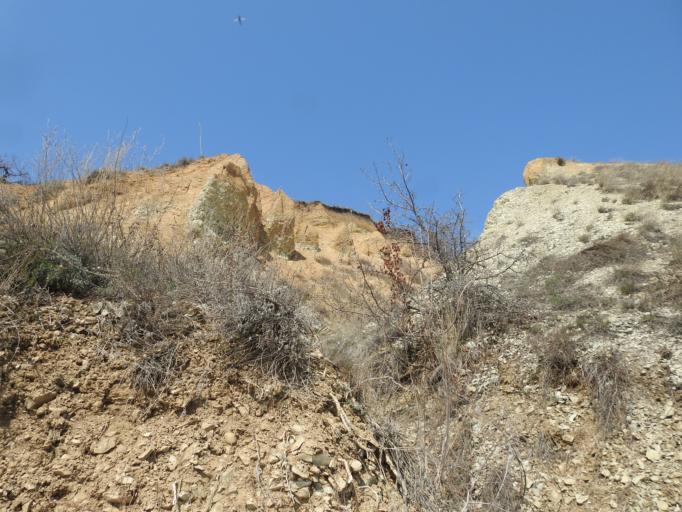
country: RU
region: Saratov
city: Voskresenskoye
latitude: 51.7930
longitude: 46.8597
